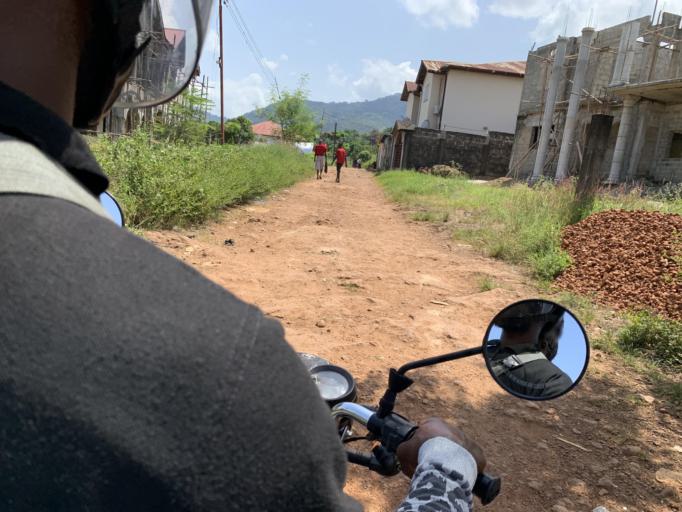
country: SL
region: Western Area
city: Hastings
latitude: 8.3730
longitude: -13.1321
